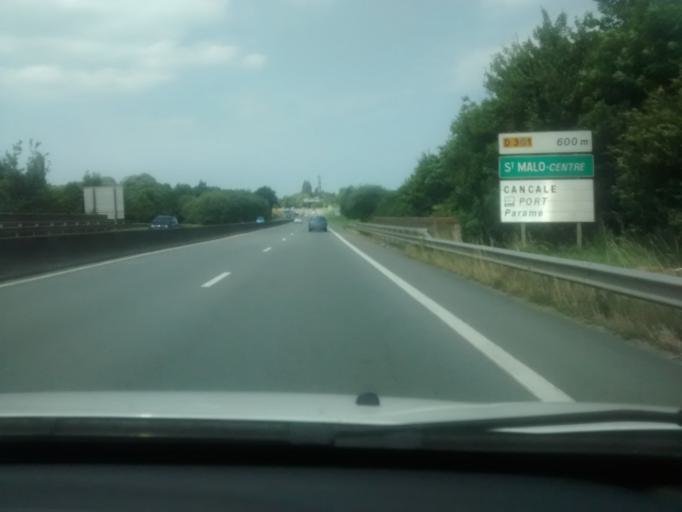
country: FR
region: Brittany
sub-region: Departement d'Ille-et-Vilaine
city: Saint-Jouan-des-Guerets
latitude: 48.6154
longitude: -1.9840
